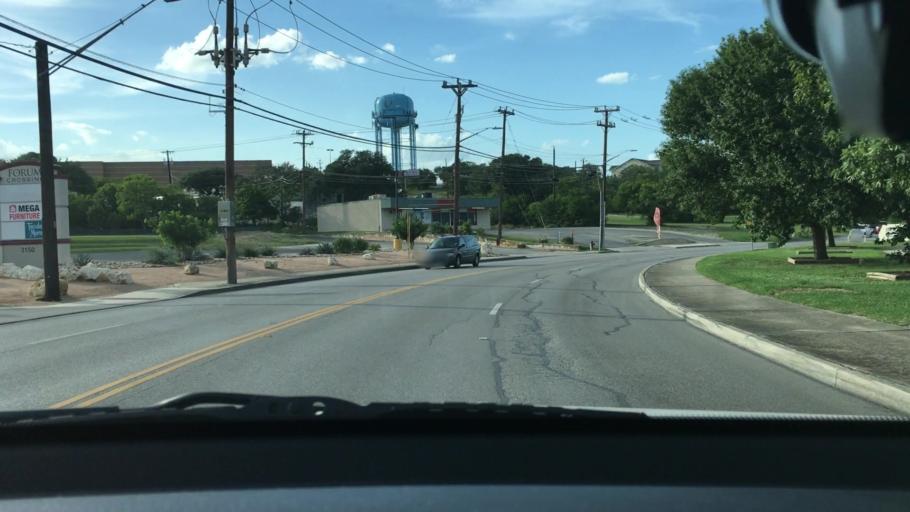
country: US
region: Texas
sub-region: Bexar County
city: Live Oak
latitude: 29.5614
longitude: -98.3247
